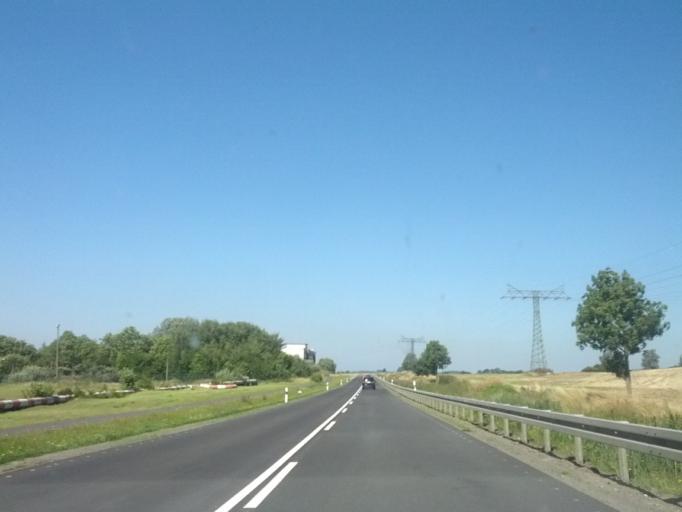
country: DE
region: Mecklenburg-Vorpommern
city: Sagard
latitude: 54.5015
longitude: 13.5601
